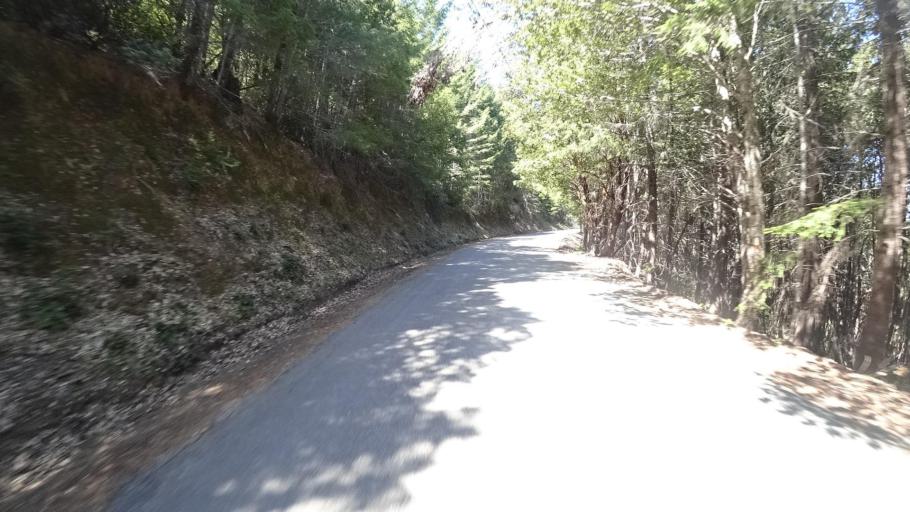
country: US
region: California
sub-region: Humboldt County
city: Redway
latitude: 40.1559
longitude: -124.0520
